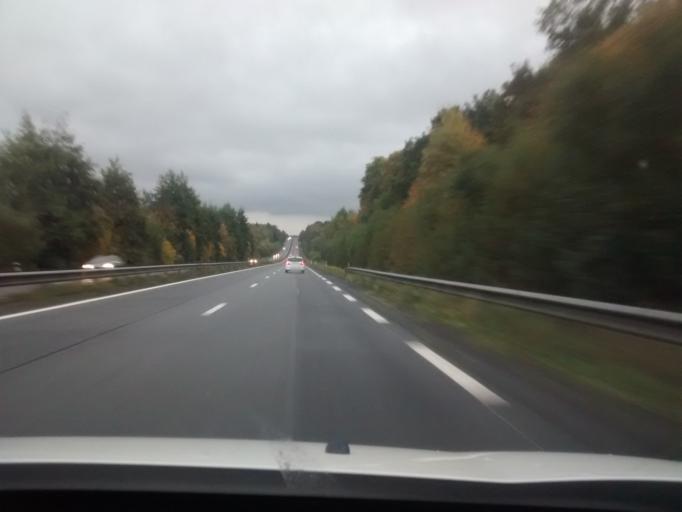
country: FR
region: Brittany
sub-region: Departement d'Ille-et-Vilaine
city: Miniac-Morvan
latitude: 48.5110
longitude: -1.9113
